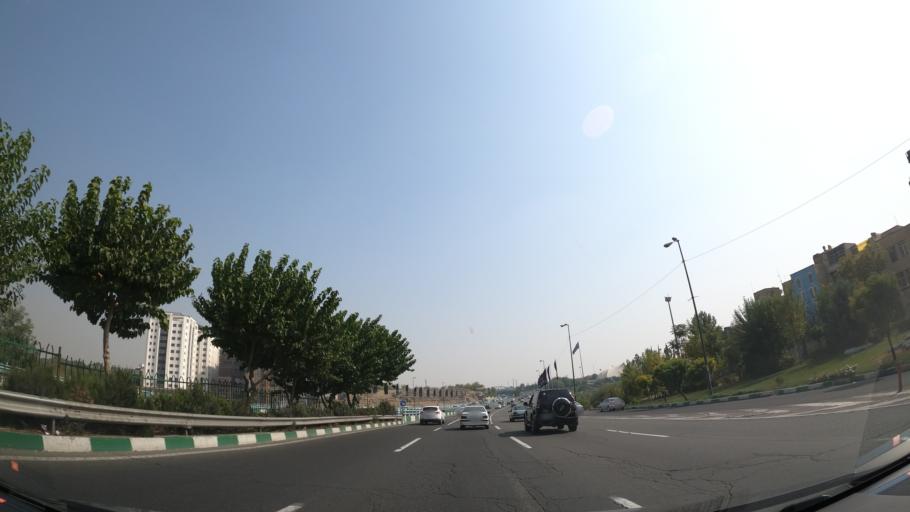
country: IR
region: Tehran
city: Shahr-e Qods
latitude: 35.7562
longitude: 51.2683
